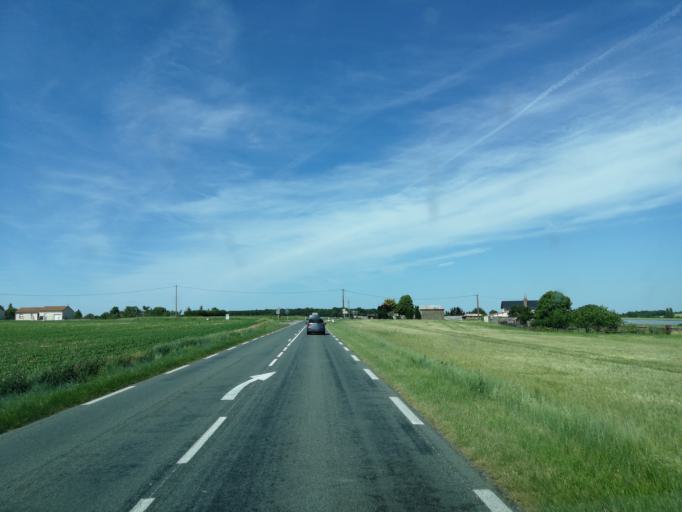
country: FR
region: Poitou-Charentes
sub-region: Departement de la Vienne
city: Loudun
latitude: 47.0338
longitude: 0.1215
